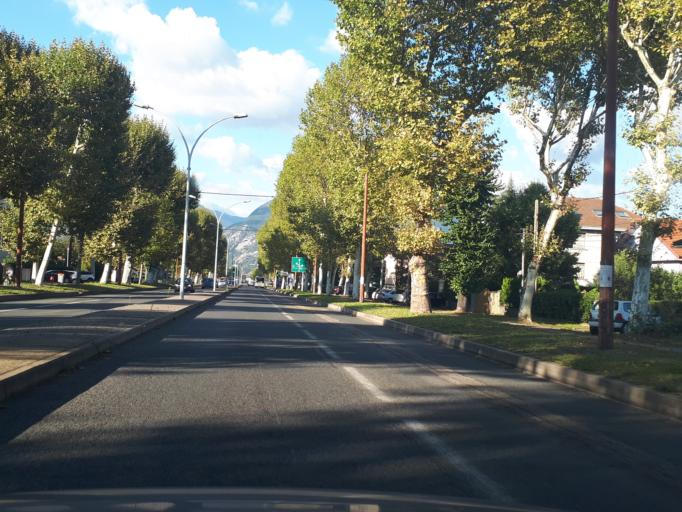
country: FR
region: Rhone-Alpes
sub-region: Departement de l'Isere
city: Grenoble
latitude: 45.1549
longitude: 5.7080
